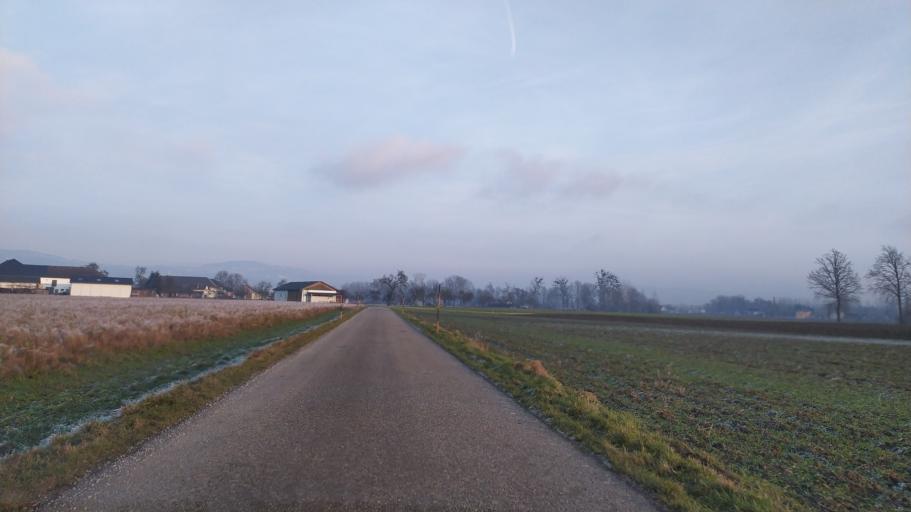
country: AT
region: Upper Austria
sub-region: Politischer Bezirk Urfahr-Umgebung
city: Goldworth
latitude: 48.3280
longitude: 14.1231
